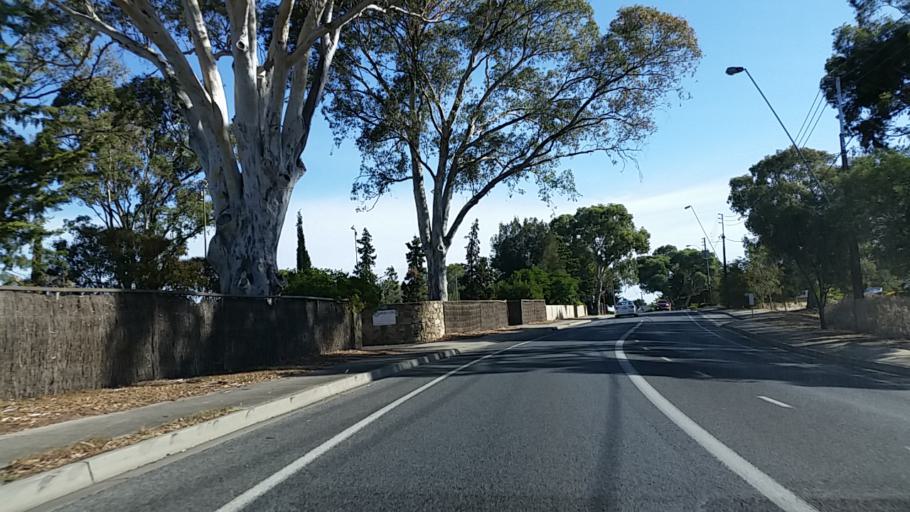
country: AU
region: South Australia
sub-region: Tea Tree Gully
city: Hope Valley
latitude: -34.8426
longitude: 138.7201
